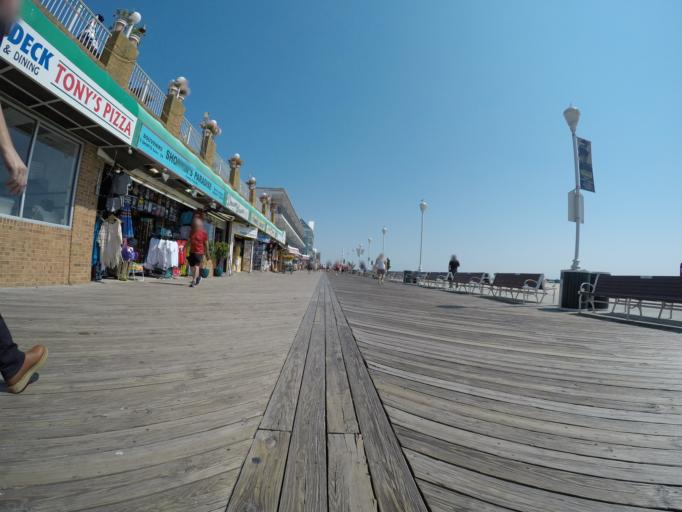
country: US
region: Maryland
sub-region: Worcester County
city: Ocean City
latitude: 38.3315
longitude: -75.0850
